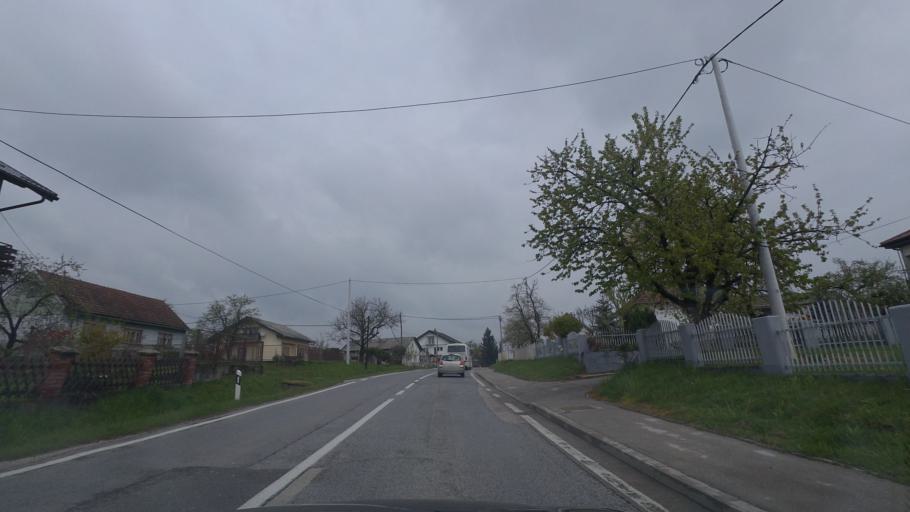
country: HR
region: Zagrebacka
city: Jastrebarsko
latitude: 45.5841
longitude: 15.5948
